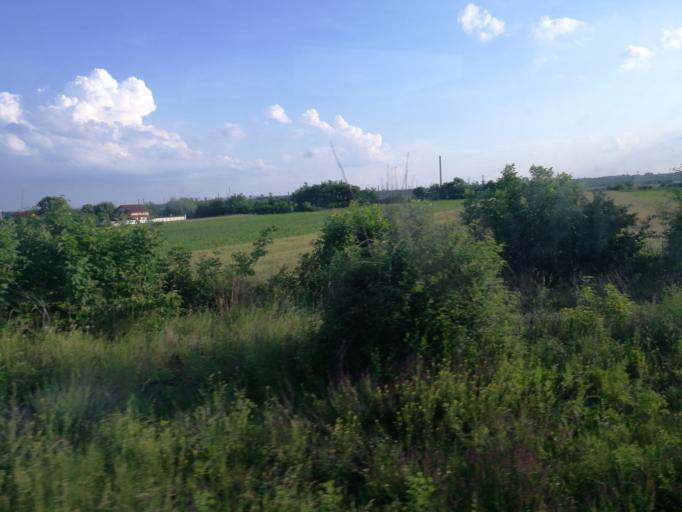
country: RO
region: Arges
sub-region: Oras Stefanesti
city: Golesti
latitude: 44.8380
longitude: 24.9537
